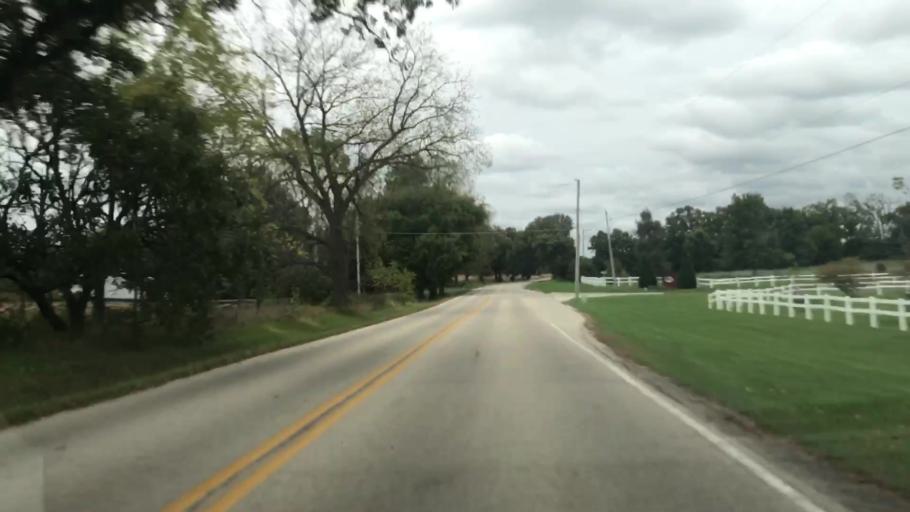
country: US
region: Wisconsin
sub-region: Waukesha County
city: North Prairie
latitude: 42.8976
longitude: -88.3969
